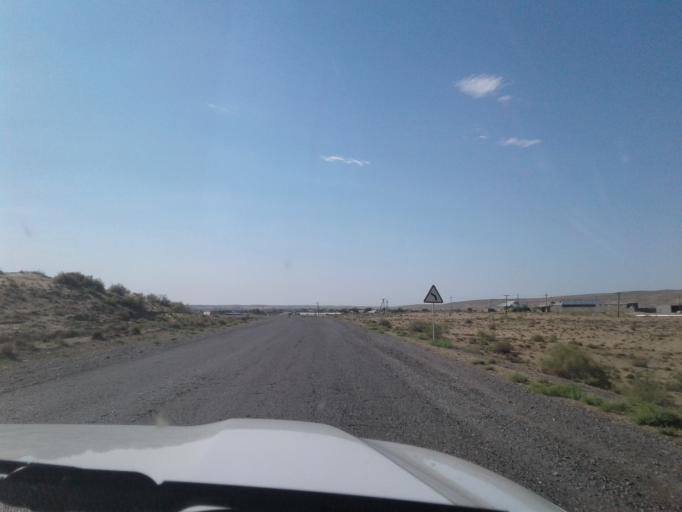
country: TM
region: Mary
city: Yoloeten
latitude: 36.5867
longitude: 62.5244
